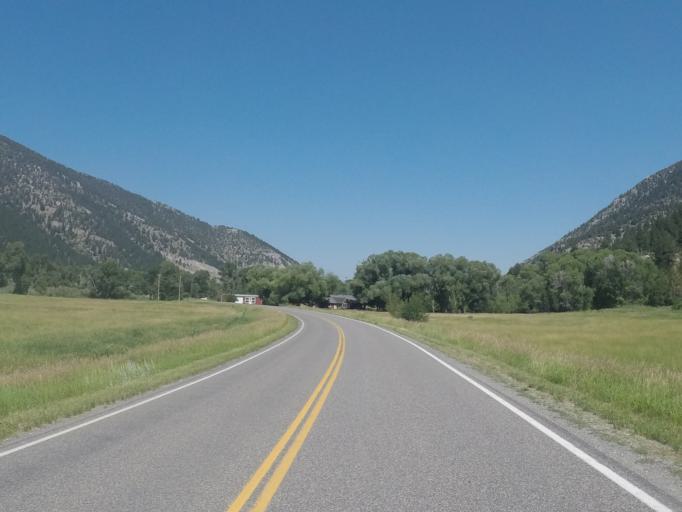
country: US
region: Montana
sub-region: Park County
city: Livingston
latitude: 45.5949
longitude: -110.5621
